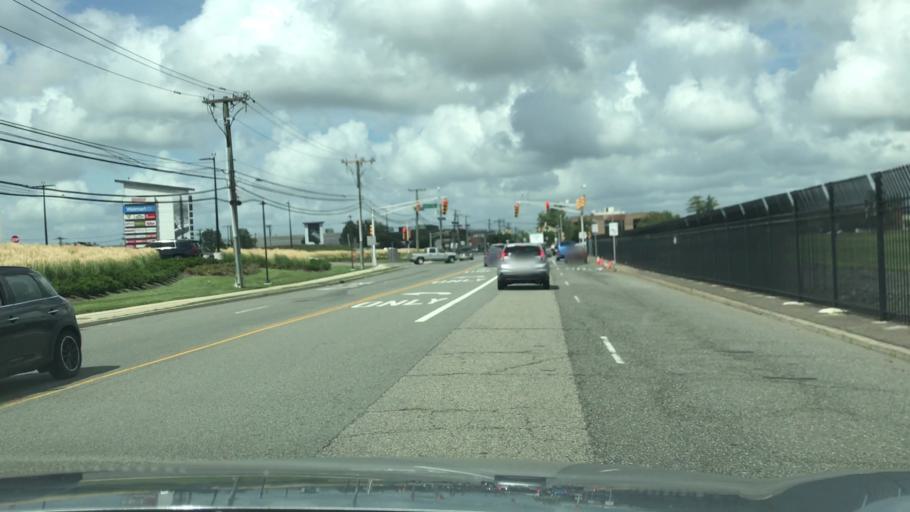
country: US
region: New Jersey
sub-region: Bergen County
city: Little Ferry
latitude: 40.8597
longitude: -74.0605
